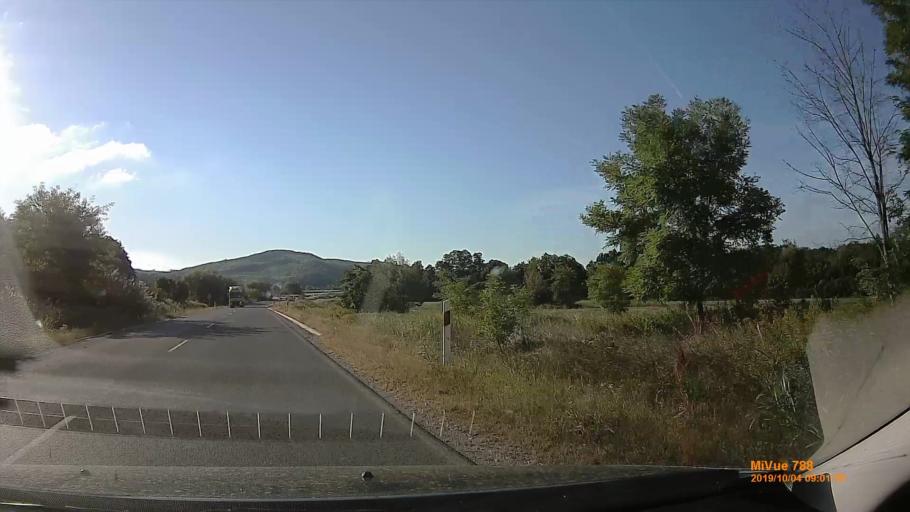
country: HU
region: Somogy
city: Karad
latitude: 46.7377
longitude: 17.7752
